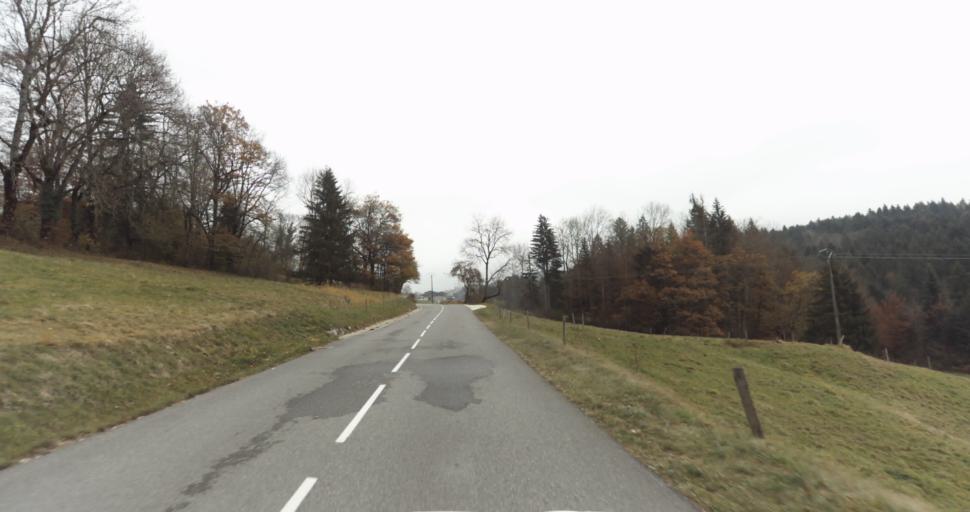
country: FR
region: Rhone-Alpes
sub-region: Departement de la Haute-Savoie
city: Gruffy
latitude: 45.7598
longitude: 6.1192
